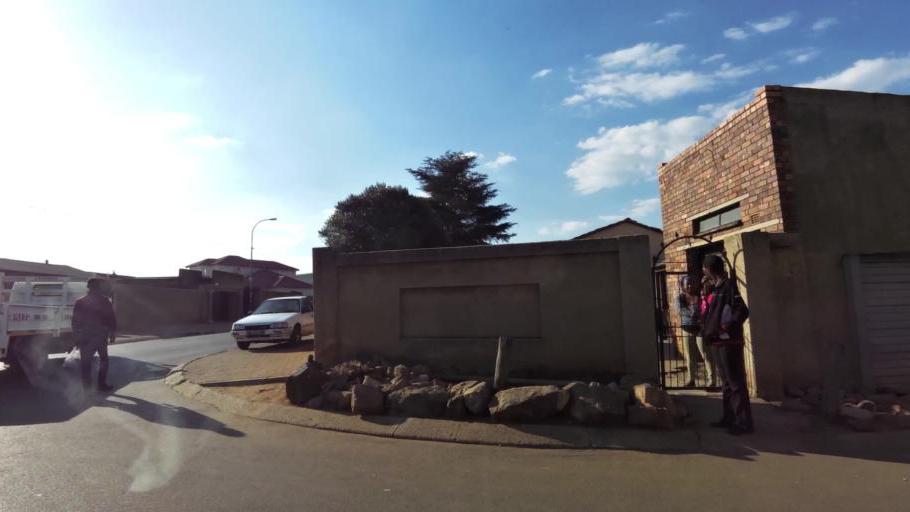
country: ZA
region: Gauteng
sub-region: City of Johannesburg Metropolitan Municipality
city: Roodepoort
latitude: -26.2162
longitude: 27.8755
